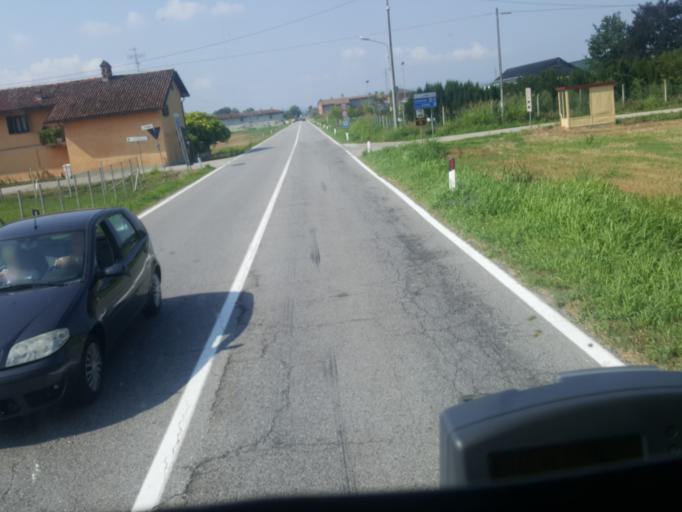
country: IT
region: Piedmont
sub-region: Provincia di Cuneo
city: Vaccheria
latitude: 44.7411
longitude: 8.0562
